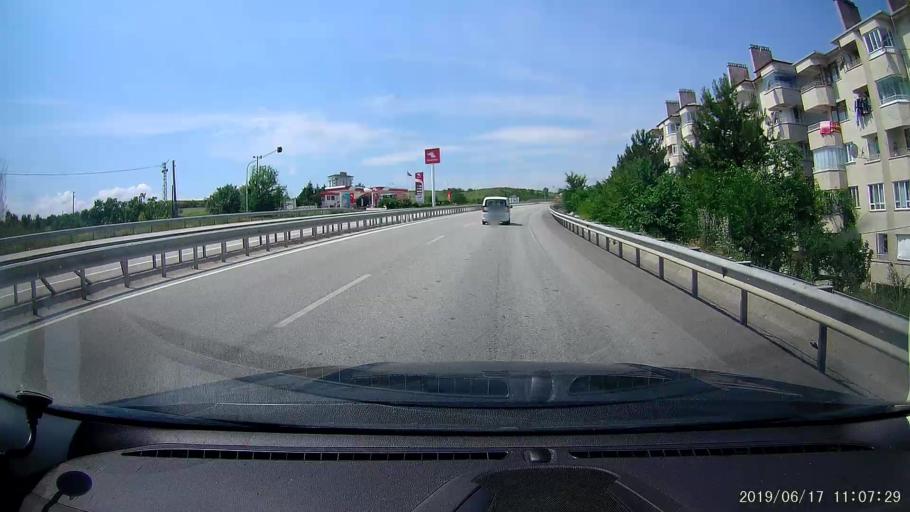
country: TR
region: Kastamonu
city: Tosya
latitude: 41.0020
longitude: 34.0544
